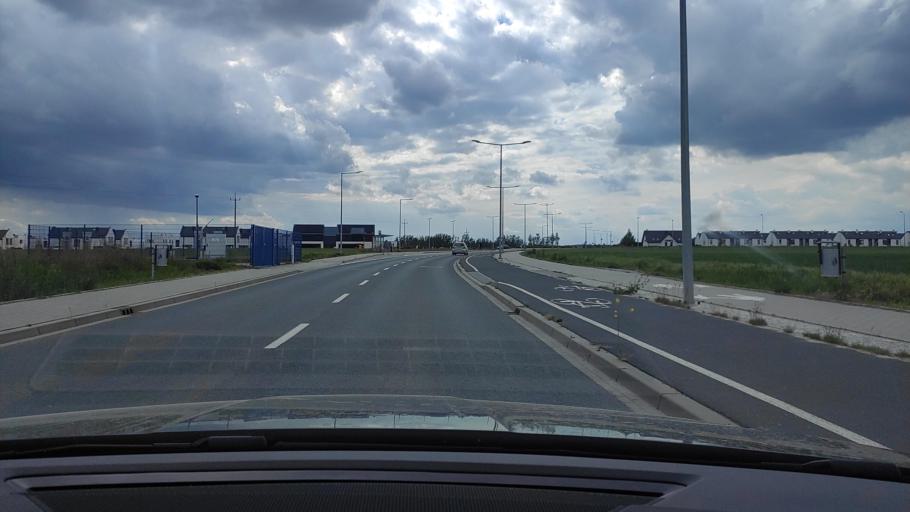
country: PL
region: Greater Poland Voivodeship
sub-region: Powiat poznanski
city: Swarzedz
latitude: 52.3808
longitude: 17.0694
